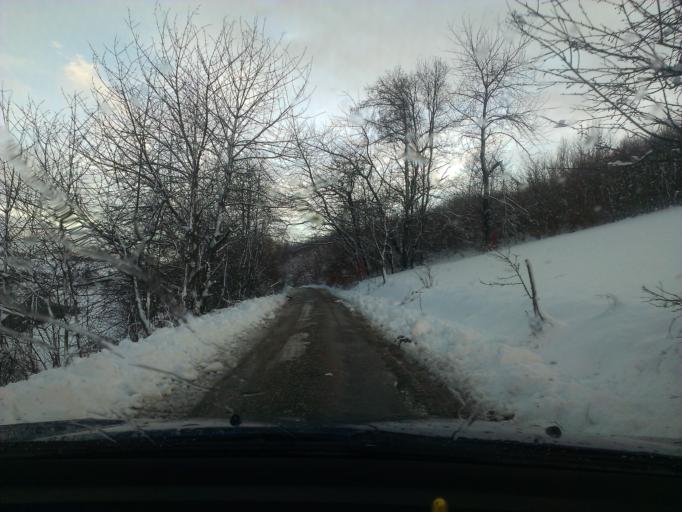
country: SK
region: Trnavsky
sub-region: Okres Trnava
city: Piestany
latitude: 48.6356
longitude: 17.9649
